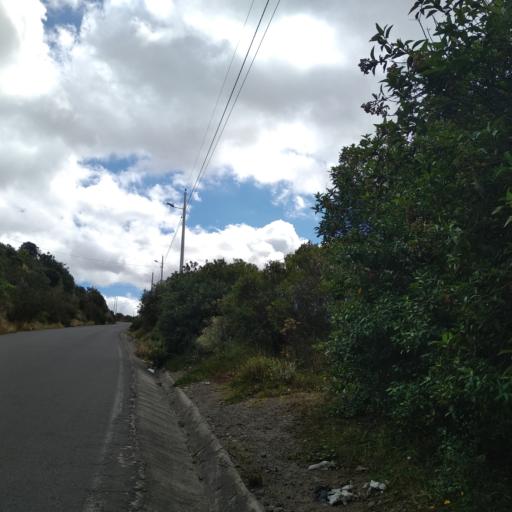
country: EC
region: Cotopaxi
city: Saquisili
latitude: -0.7520
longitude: -78.7286
